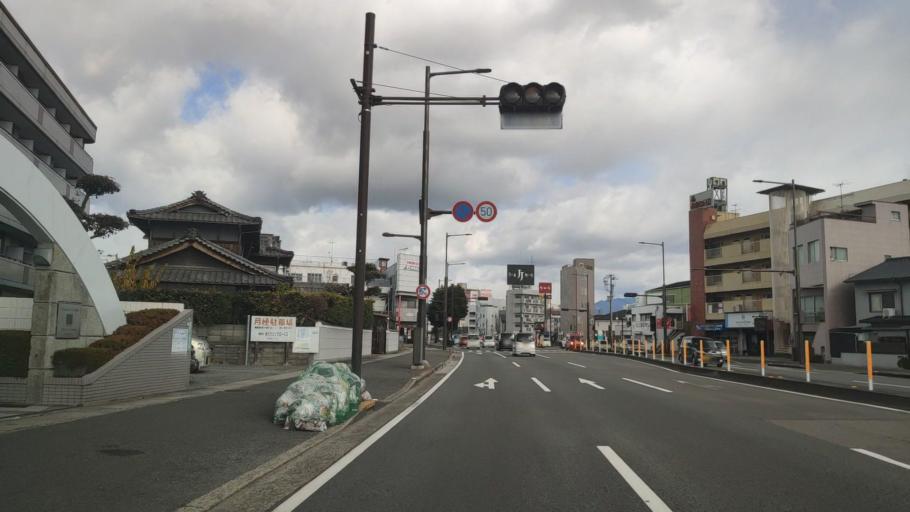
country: JP
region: Ehime
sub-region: Shikoku-chuo Shi
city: Matsuyama
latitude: 33.8245
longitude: 132.7580
